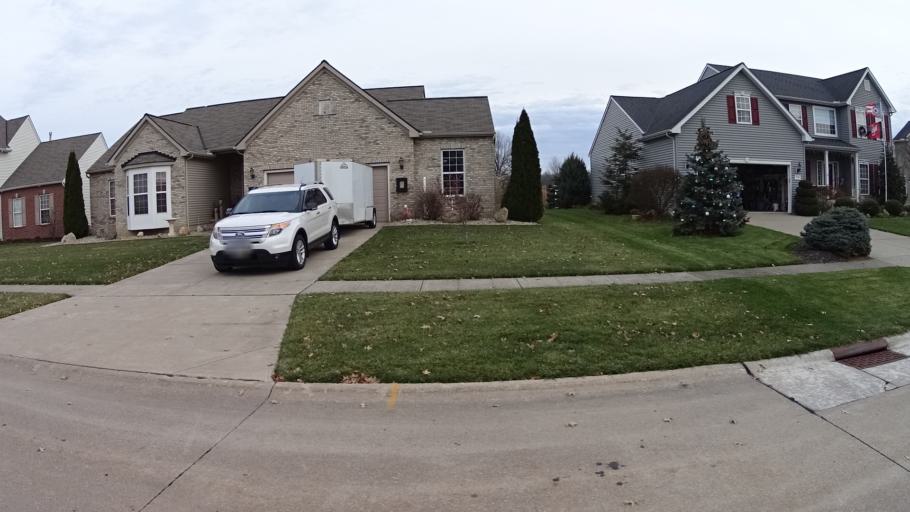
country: US
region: Ohio
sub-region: Lorain County
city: North Ridgeville
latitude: 41.4028
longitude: -82.0352
